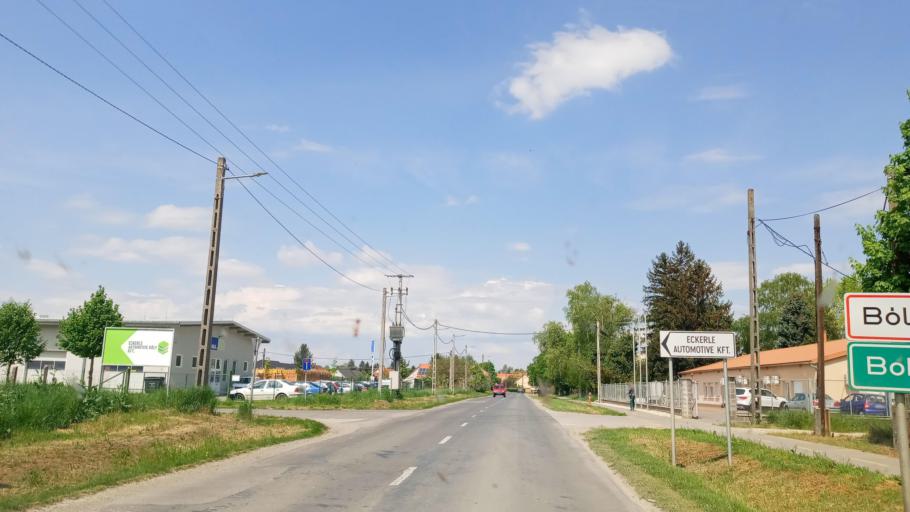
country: HU
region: Baranya
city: Boly
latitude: 45.9602
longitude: 18.5248
